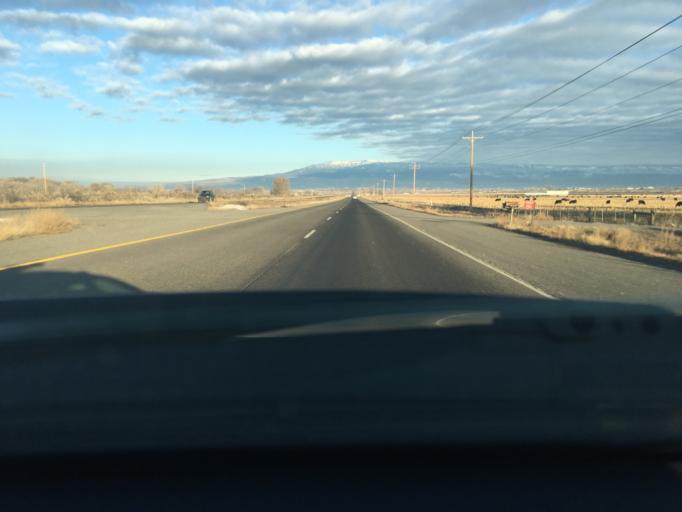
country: US
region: Colorado
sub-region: Montrose County
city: Olathe
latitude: 38.6745
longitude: -108.0031
